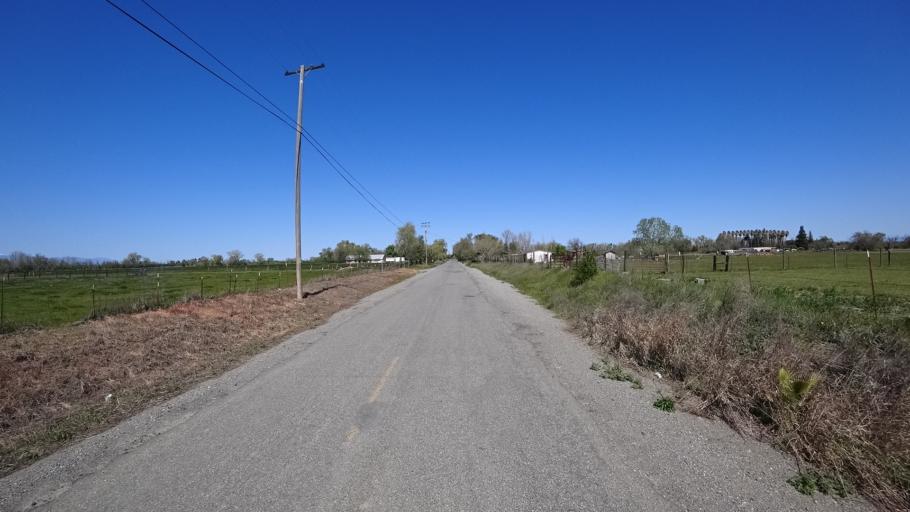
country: US
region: California
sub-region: Glenn County
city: Orland
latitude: 39.7690
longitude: -122.2478
